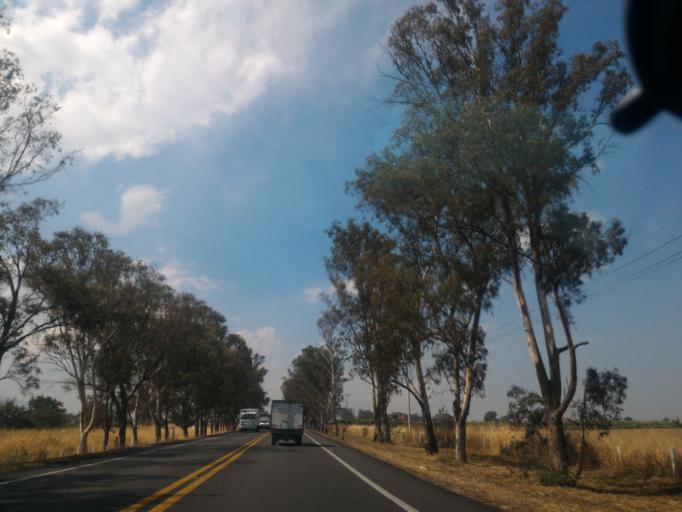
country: MX
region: Jalisco
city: Tuxpan
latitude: 19.5518
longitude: -103.4354
